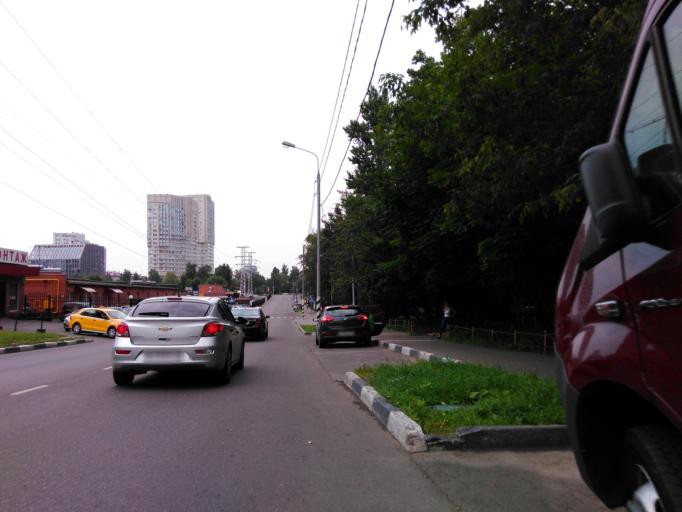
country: RU
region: Moskovskaya
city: Semenovskoye
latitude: 55.6792
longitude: 37.5525
